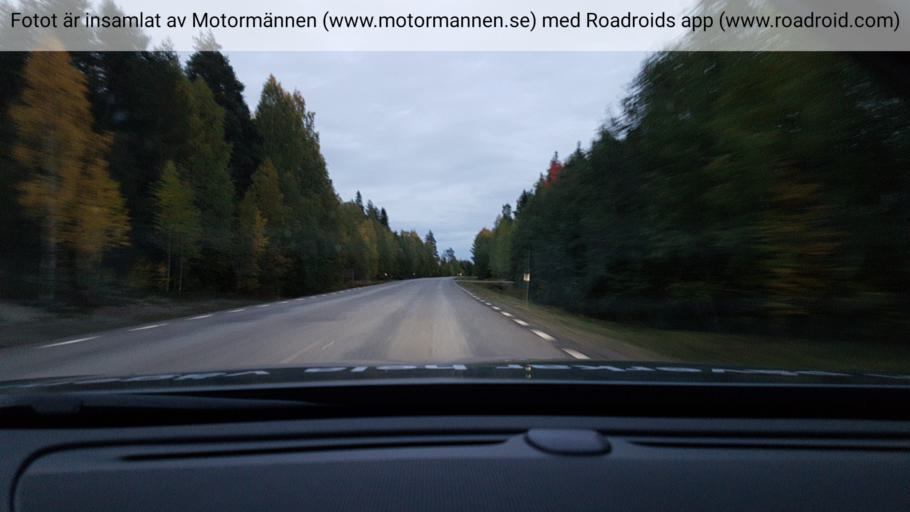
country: SE
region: Norrbotten
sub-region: Alvsbyns Kommun
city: AElvsbyn
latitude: 65.7781
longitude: 20.8359
